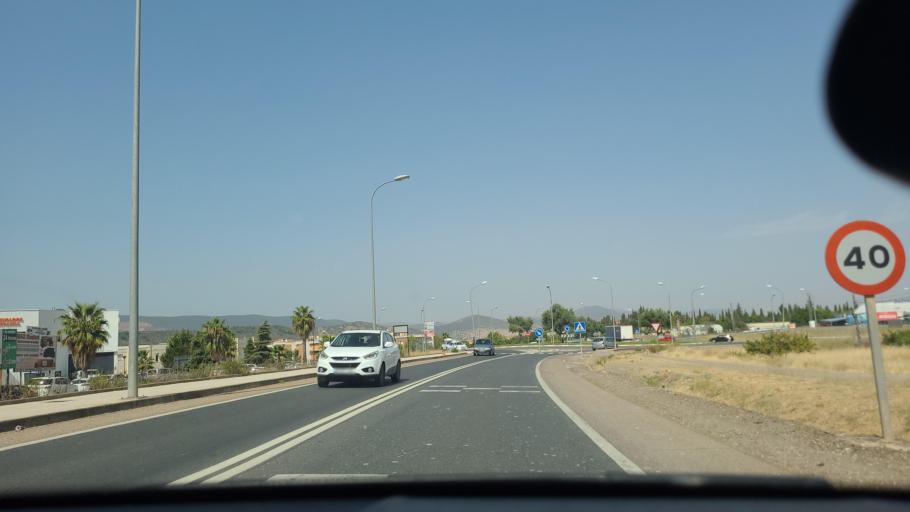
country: ES
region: Extremadura
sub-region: Provincia de Badajoz
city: Zafra
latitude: 38.4309
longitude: -6.4193
